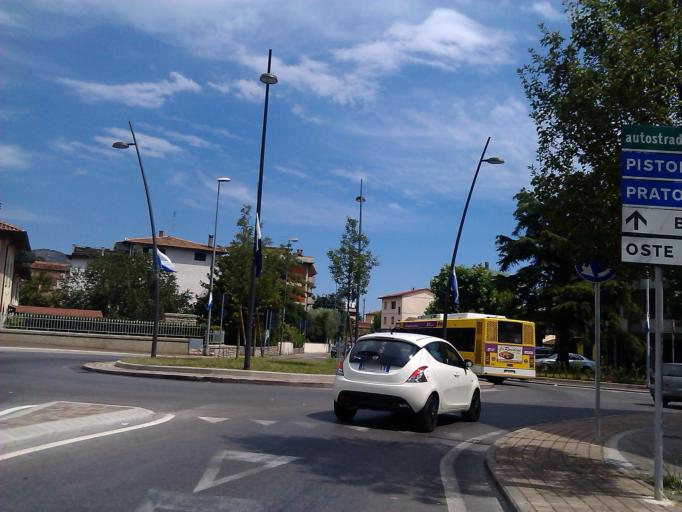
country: IT
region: Tuscany
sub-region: Provincia di Prato
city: Montemurlo
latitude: 43.9296
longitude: 11.0321
